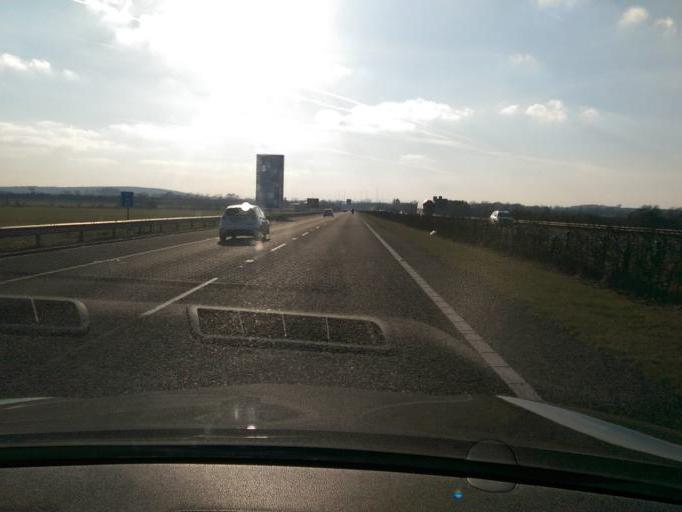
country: IE
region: Leinster
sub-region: Kildare
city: Cherryville
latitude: 53.1486
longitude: -6.9964
